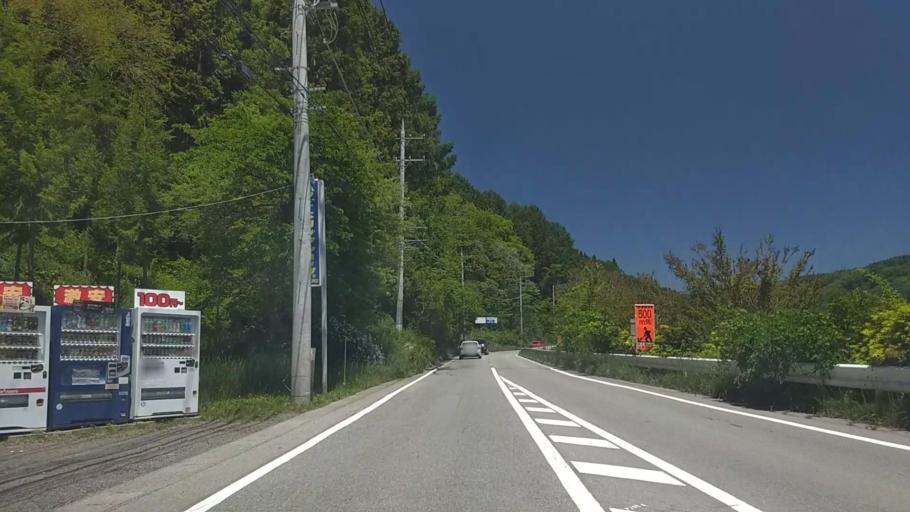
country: JP
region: Yamanashi
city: Nirasaki
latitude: 35.8649
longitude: 138.4272
